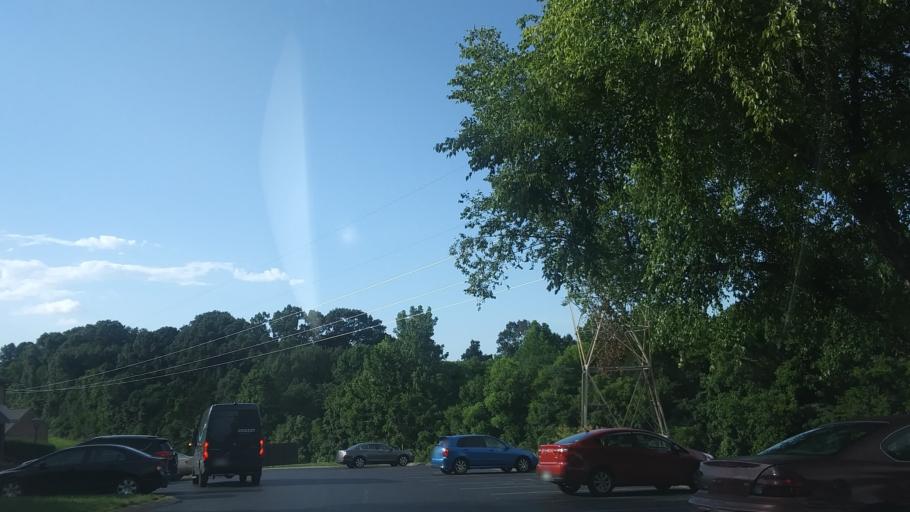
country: US
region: Tennessee
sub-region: Rutherford County
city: La Vergne
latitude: 36.0843
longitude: -86.6410
